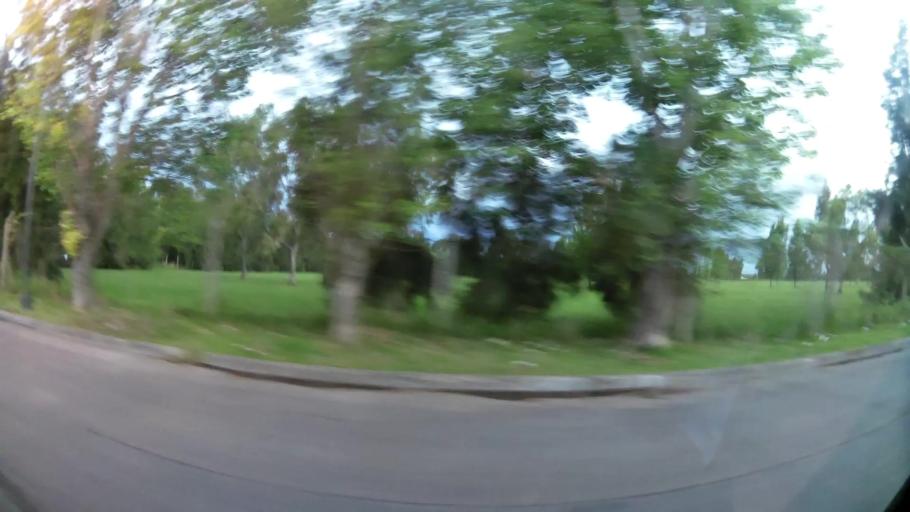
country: AR
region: Buenos Aires
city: San Nicolas de los Arroyos
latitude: -33.3461
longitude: -60.1929
